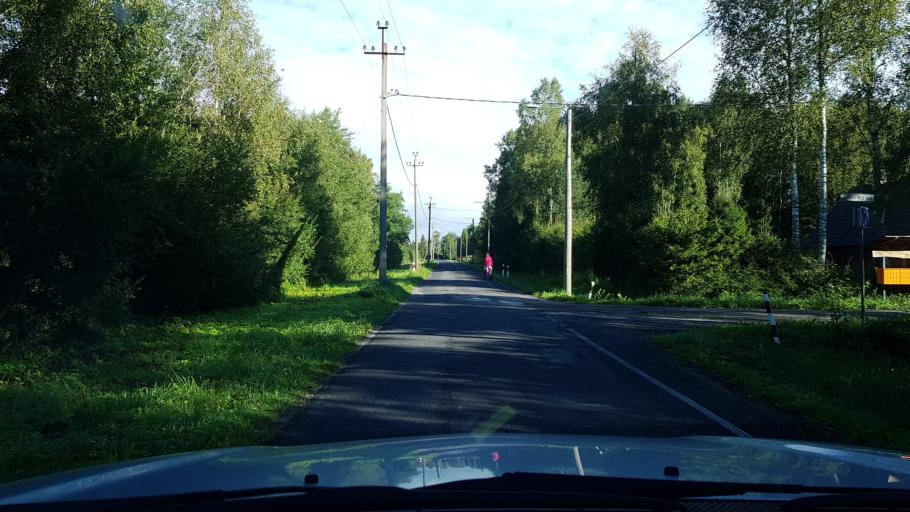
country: EE
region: Harju
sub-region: Rae vald
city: Vaida
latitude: 59.2946
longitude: 24.9182
